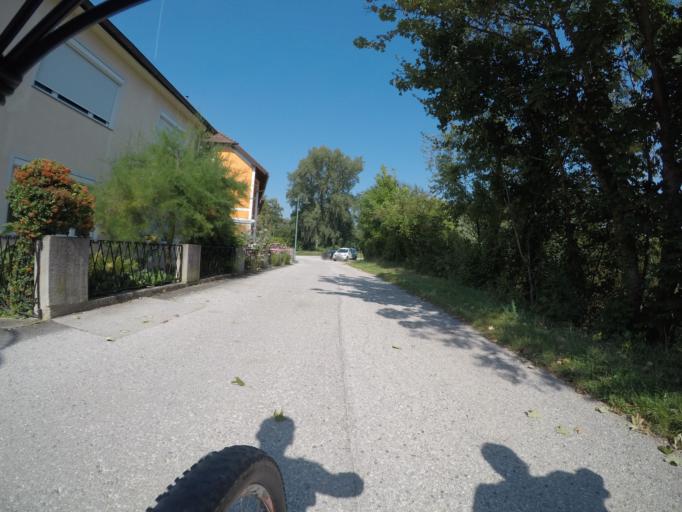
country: AT
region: Lower Austria
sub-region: Politischer Bezirk Baden
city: Berndorf
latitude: 47.9371
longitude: 16.1423
